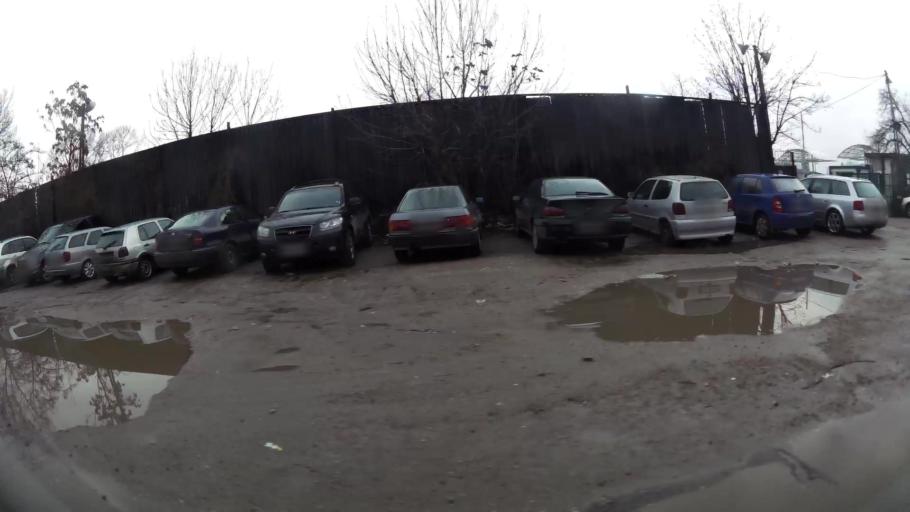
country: BG
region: Sofia-Capital
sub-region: Stolichna Obshtina
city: Sofia
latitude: 42.7194
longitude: 23.3609
